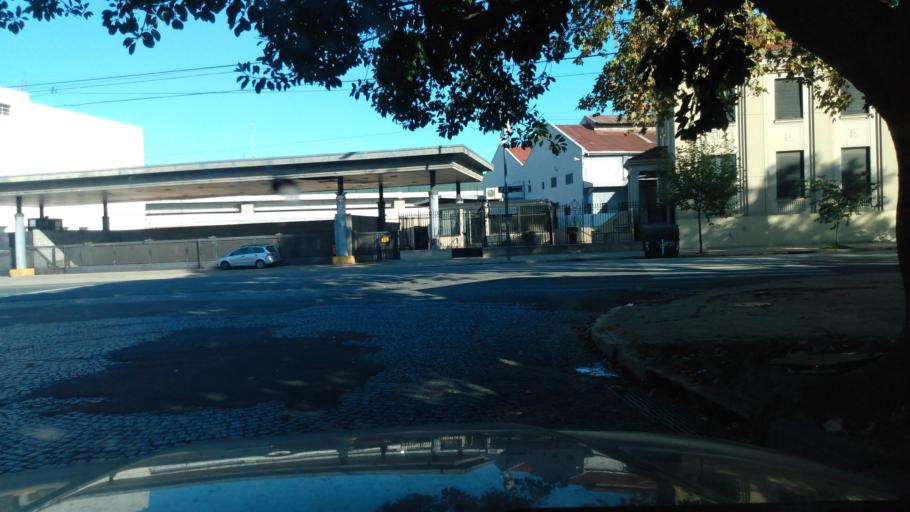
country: AR
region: Buenos Aires F.D.
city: Villa Santa Rita
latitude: -34.5960
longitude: -58.4682
